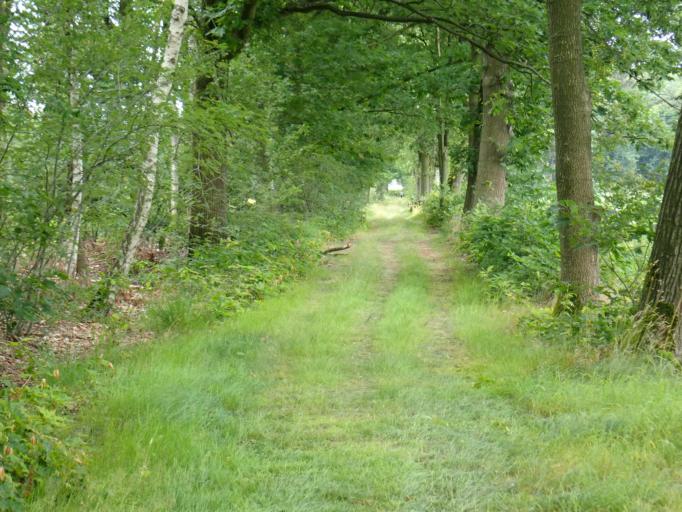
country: BE
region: Flanders
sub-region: Provincie Antwerpen
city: Merksplas
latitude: 51.3772
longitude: 4.8848
